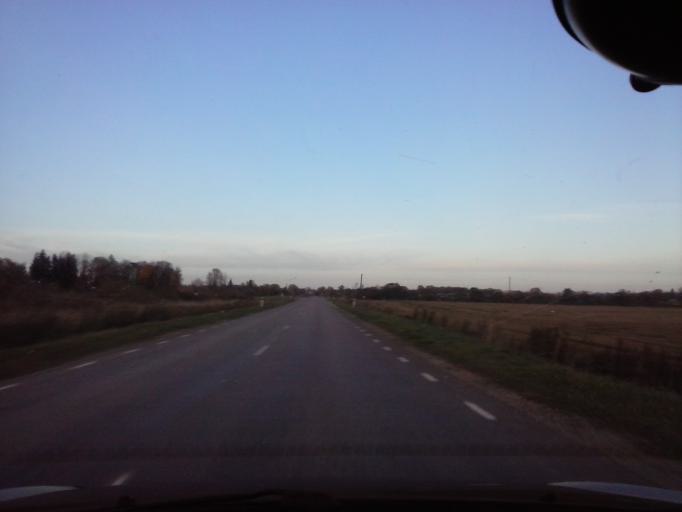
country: EE
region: Harju
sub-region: Nissi vald
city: Turba
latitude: 58.9111
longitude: 24.1468
